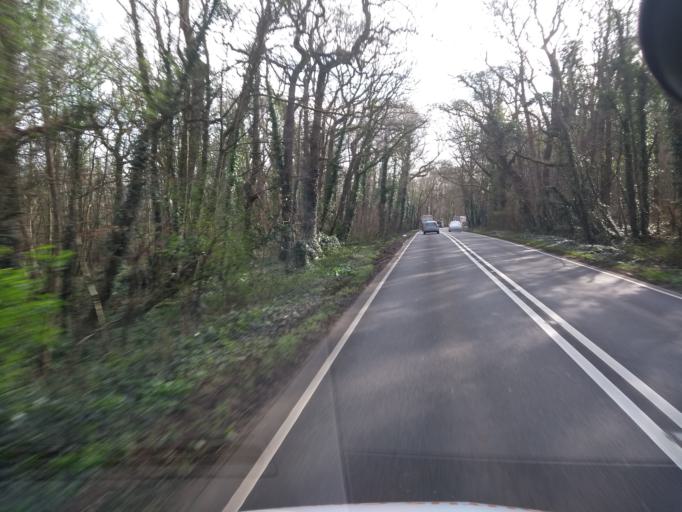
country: GB
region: England
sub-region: Somerset
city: Westonzoyland
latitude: 51.1327
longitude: -2.8478
